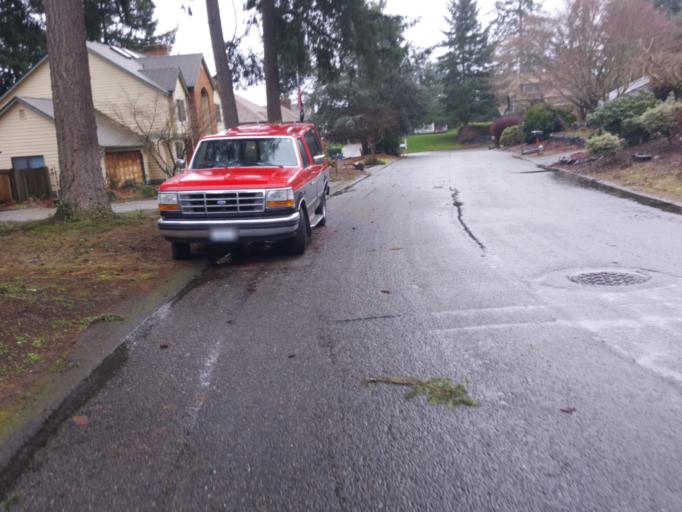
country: US
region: Washington
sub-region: Pierce County
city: University Place
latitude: 47.2058
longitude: -122.5326
